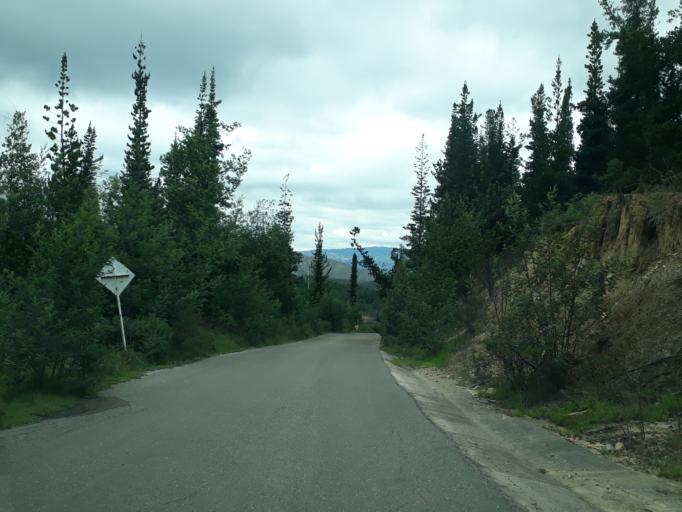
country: CO
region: Cundinamarca
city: Cucunuba
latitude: 5.2269
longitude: -73.7786
